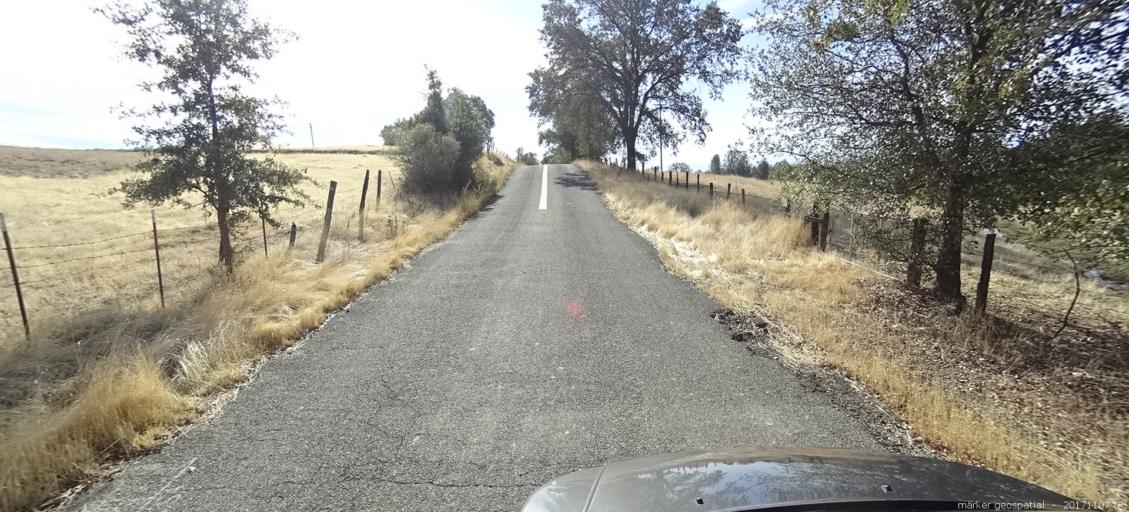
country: US
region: California
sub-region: Shasta County
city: Shasta
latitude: 40.5070
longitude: -122.5470
